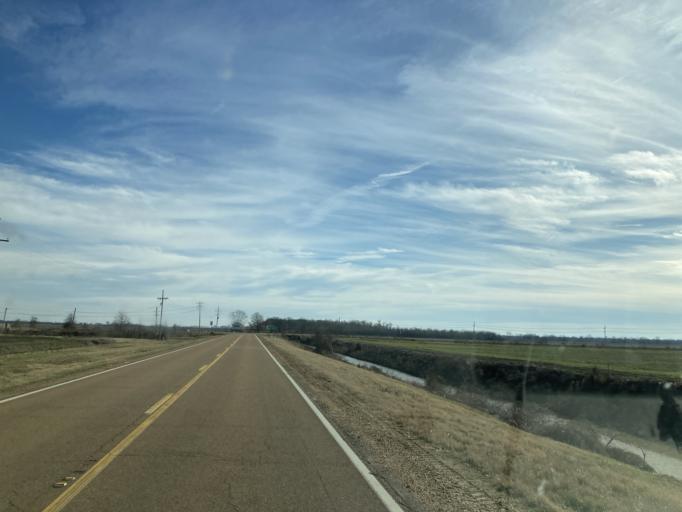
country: US
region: Mississippi
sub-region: Humphreys County
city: Belzoni
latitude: 32.9957
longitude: -90.5909
